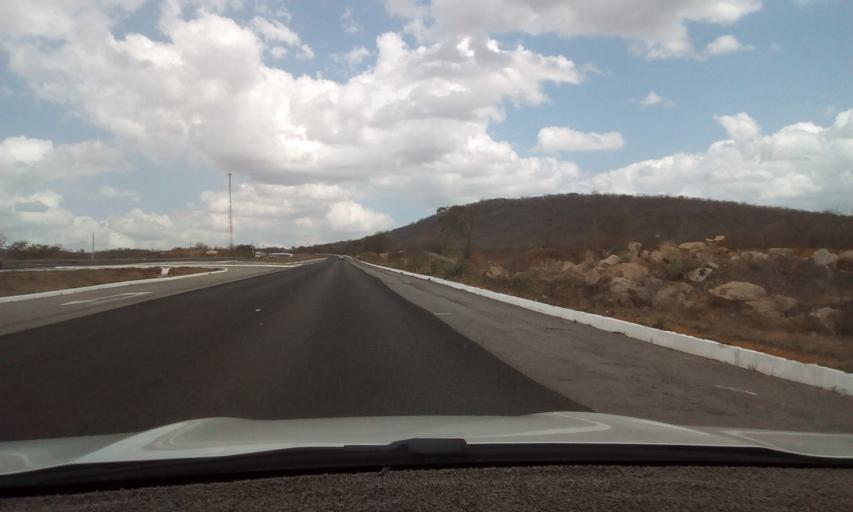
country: BR
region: Pernambuco
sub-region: Toritama
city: Toritama
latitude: -8.1177
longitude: -36.0031
